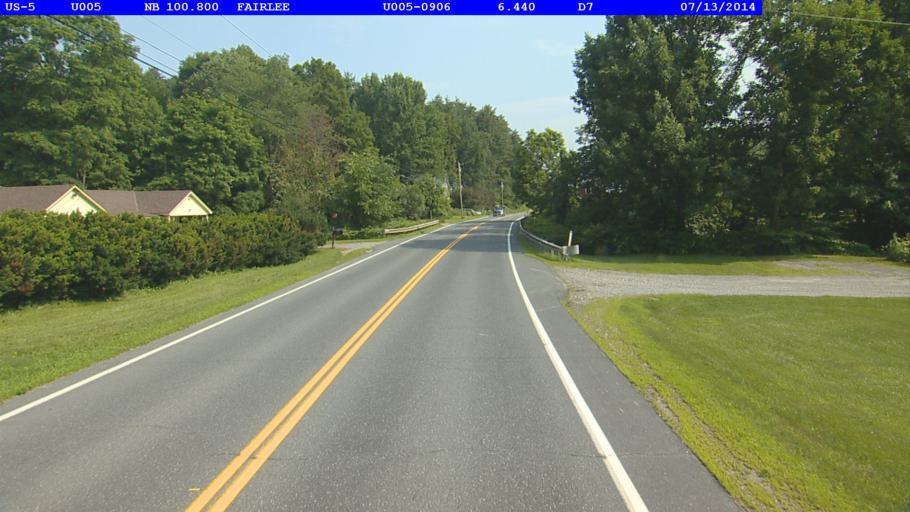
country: US
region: New Hampshire
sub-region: Grafton County
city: Orford
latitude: 43.9496
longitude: -72.1178
